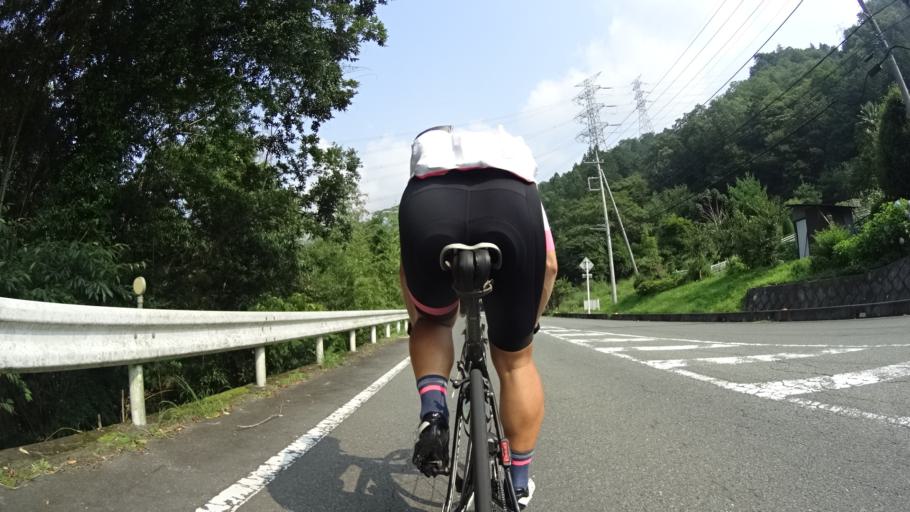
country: JP
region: Saitama
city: Chichibu
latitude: 36.0299
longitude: 138.9398
